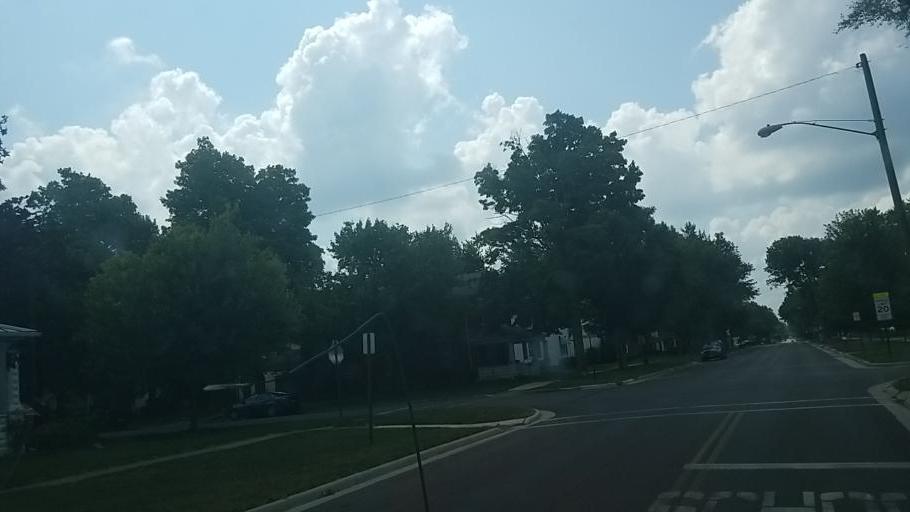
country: US
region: Ohio
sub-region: Wyandot County
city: Upper Sandusky
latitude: 40.8319
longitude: -83.2845
